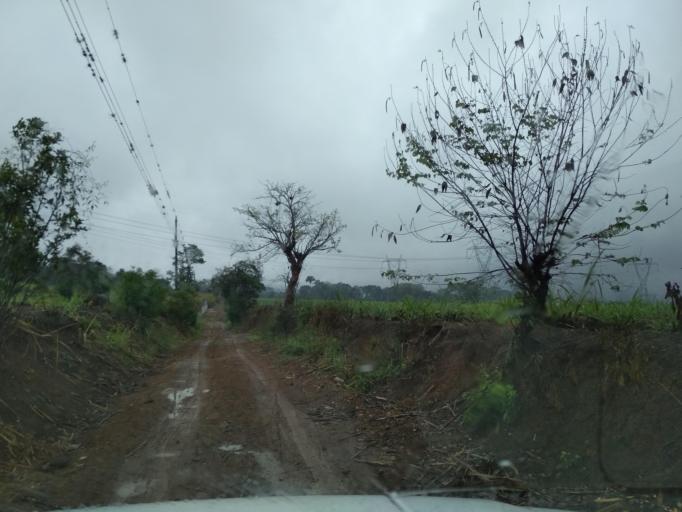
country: MX
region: Veracruz
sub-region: Amatlan de los Reyes
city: Centro de Readaptacion Social
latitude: 18.8354
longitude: -96.9312
